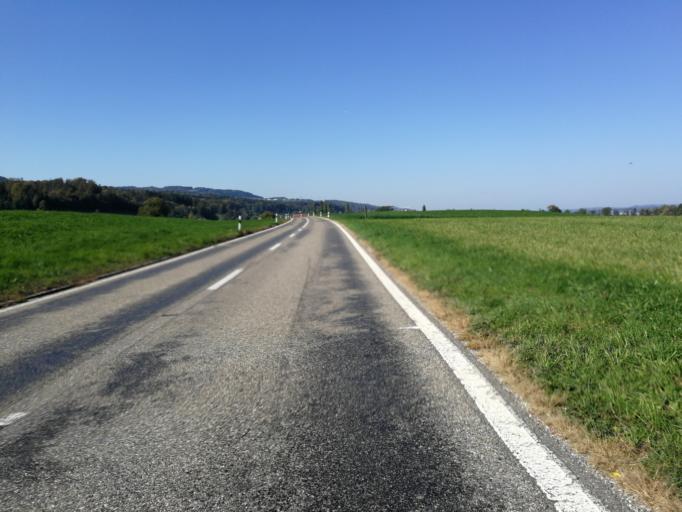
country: CH
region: Zurich
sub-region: Bezirk Uster
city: Monchaltorf
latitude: 47.3135
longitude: 8.7057
